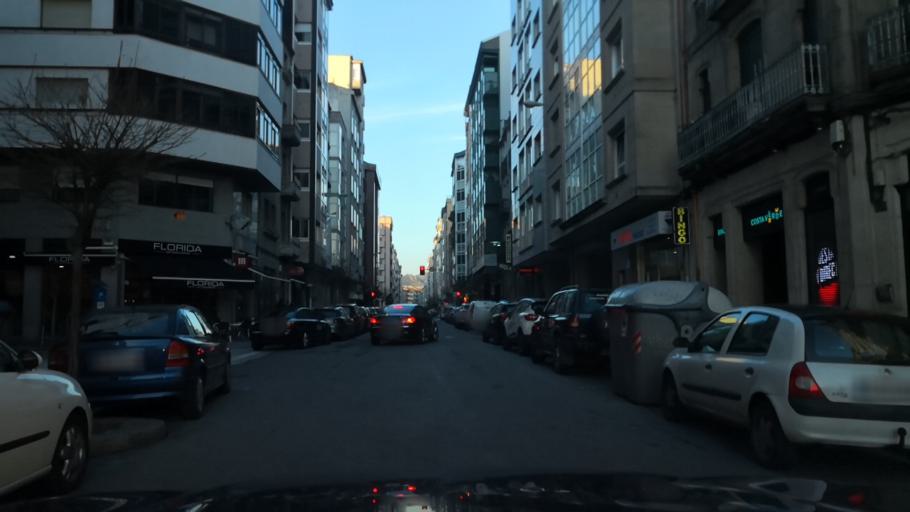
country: ES
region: Galicia
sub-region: Provincia de Ourense
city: Ourense
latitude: 42.3389
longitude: -7.8617
